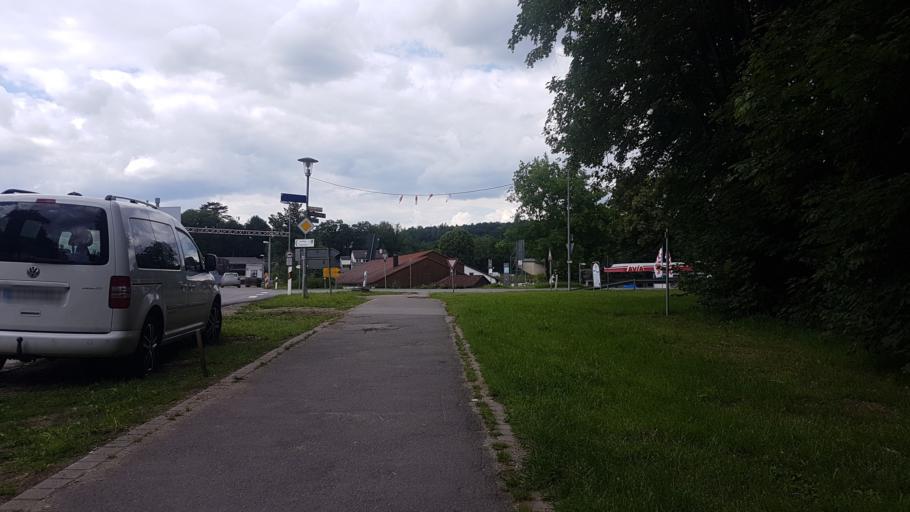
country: DE
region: Bavaria
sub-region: Regierungsbezirk Mittelfranken
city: Pappenheim
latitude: 48.9265
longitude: 10.9650
